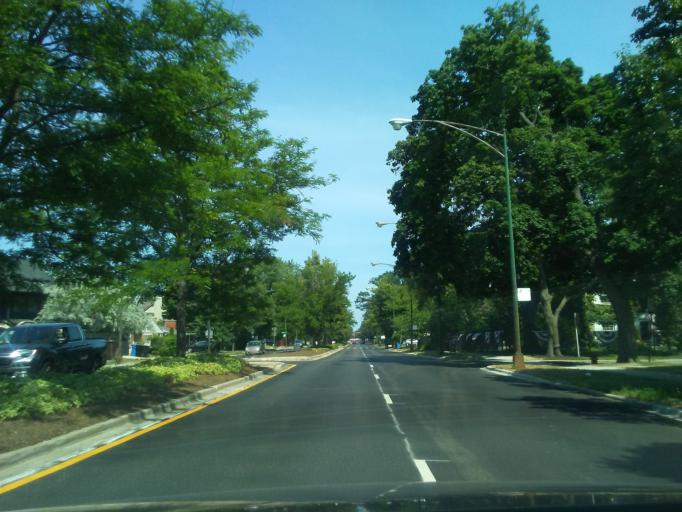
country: US
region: Illinois
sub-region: Cook County
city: Lincolnwood
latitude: 41.9899
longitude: -87.7424
